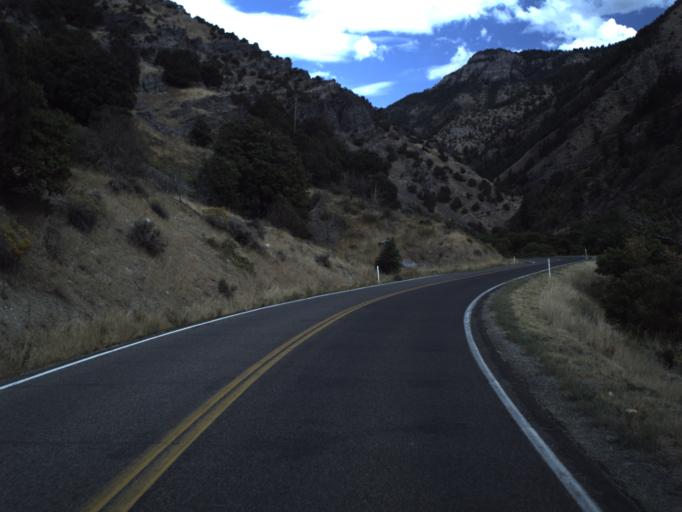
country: US
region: Utah
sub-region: Cache County
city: Hyrum
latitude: 41.6253
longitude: -111.7904
